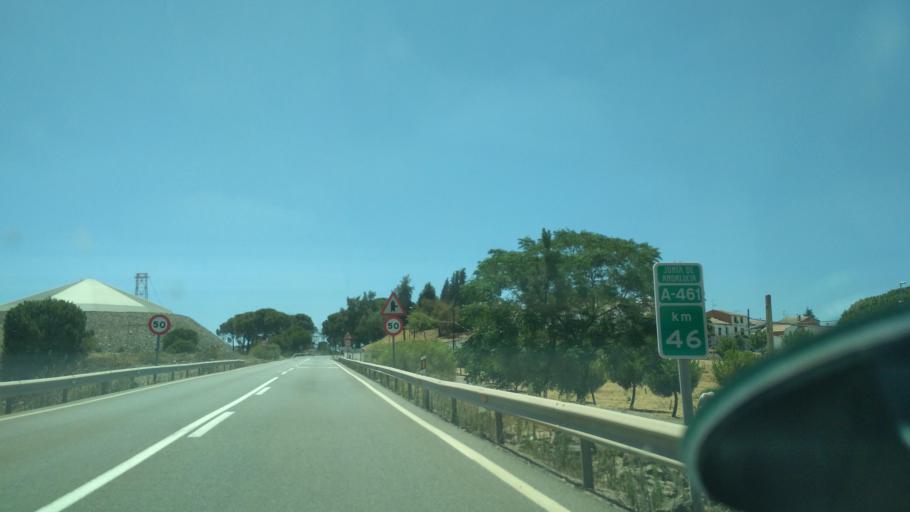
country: ES
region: Andalusia
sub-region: Provincia de Huelva
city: Nerva
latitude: 37.7150
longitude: -6.5796
